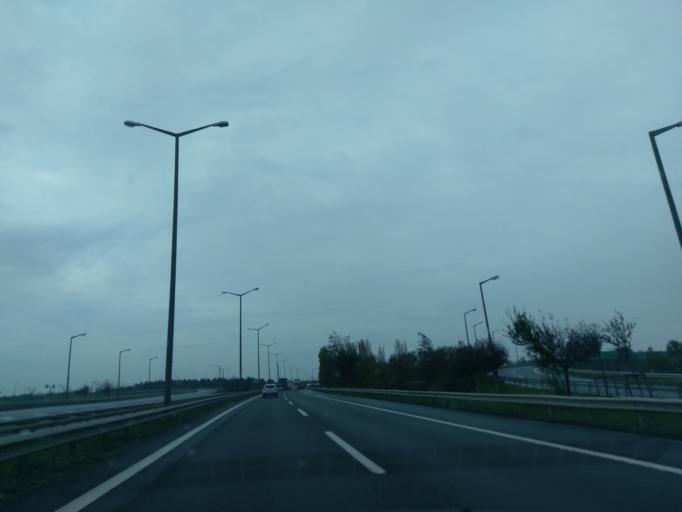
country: TR
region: Istanbul
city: Silivri
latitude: 41.1094
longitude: 28.2690
